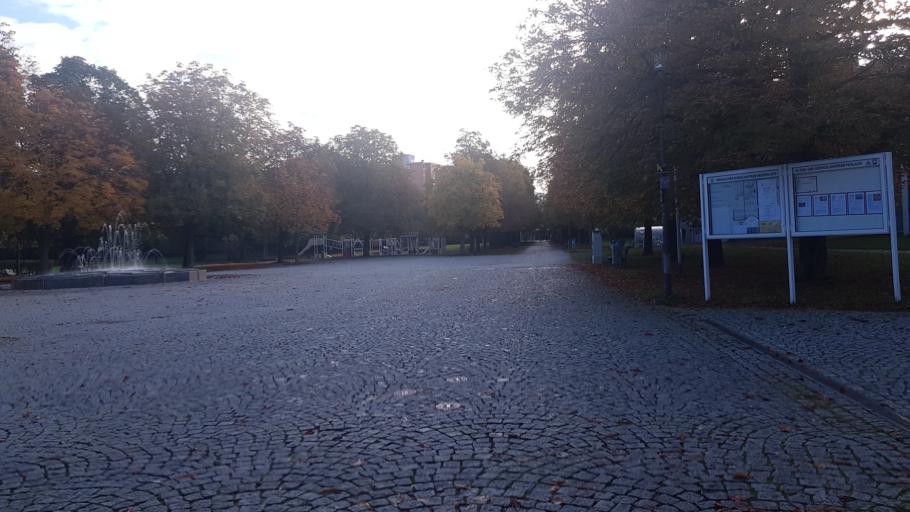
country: DE
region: Bavaria
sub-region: Upper Bavaria
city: Neubiberg
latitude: 48.1016
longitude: 11.6401
